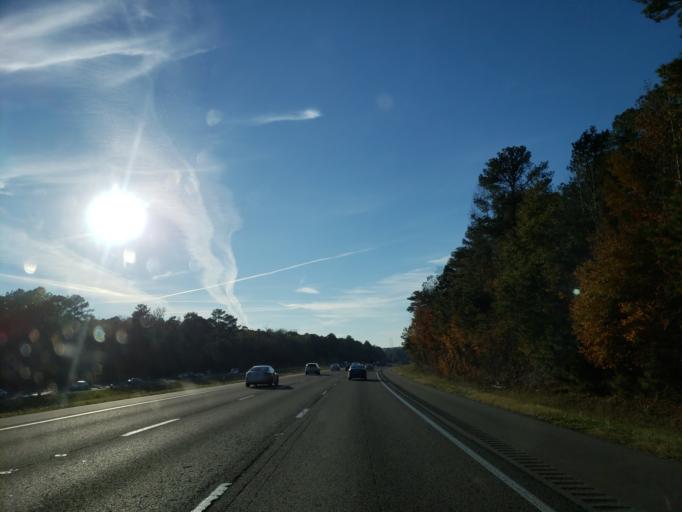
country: US
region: Alabama
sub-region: Tuscaloosa County
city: Coaling
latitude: 33.1847
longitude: -87.3420
